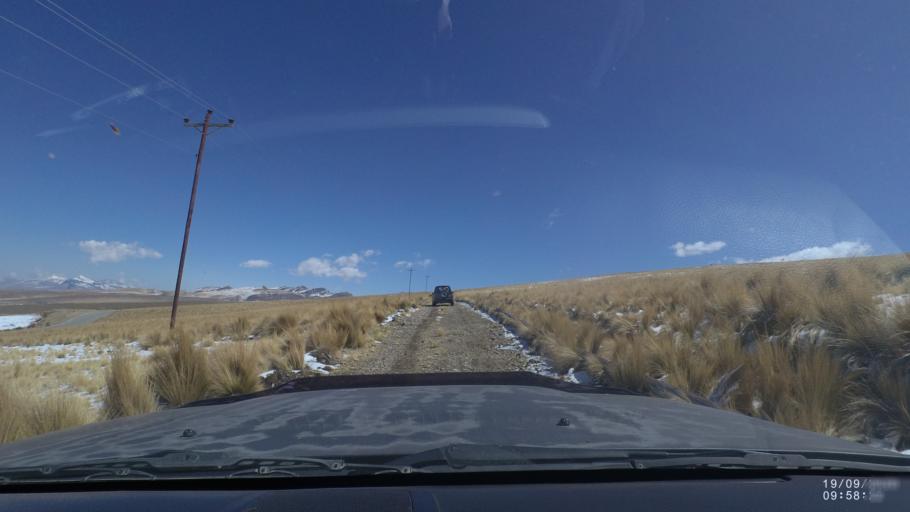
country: BO
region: Cochabamba
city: Cochabamba
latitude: -17.3100
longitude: -66.0860
